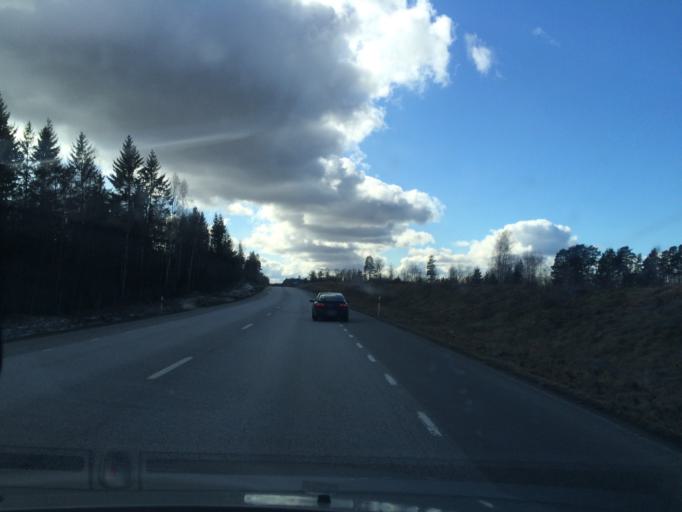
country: SE
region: Vaestra Goetaland
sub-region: Mariestads Kommun
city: Mariestad
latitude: 58.6459
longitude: 13.7130
